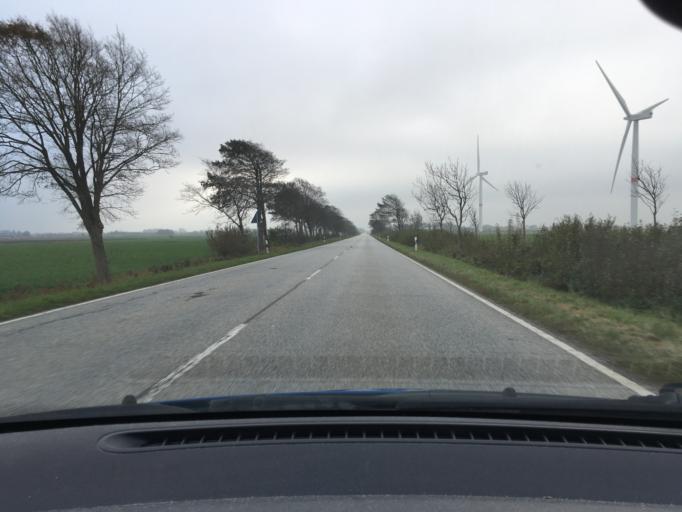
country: DE
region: Schleswig-Holstein
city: Braderup
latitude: 54.8262
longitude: 8.8880
